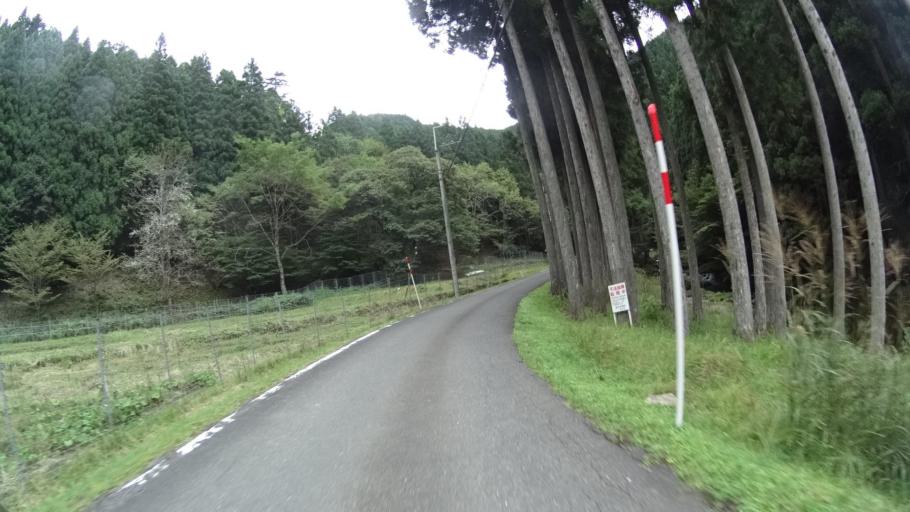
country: JP
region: Shiga Prefecture
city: Kitahama
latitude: 35.2331
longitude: 135.7903
